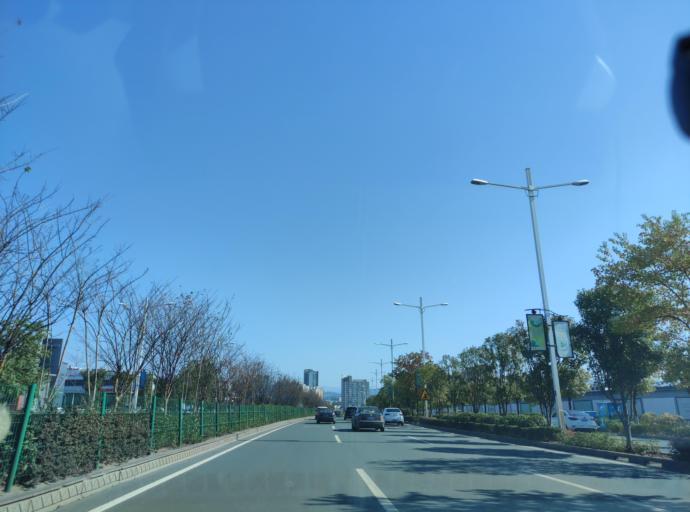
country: CN
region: Jiangxi Sheng
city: Pingxiang
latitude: 27.6552
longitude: 113.8571
